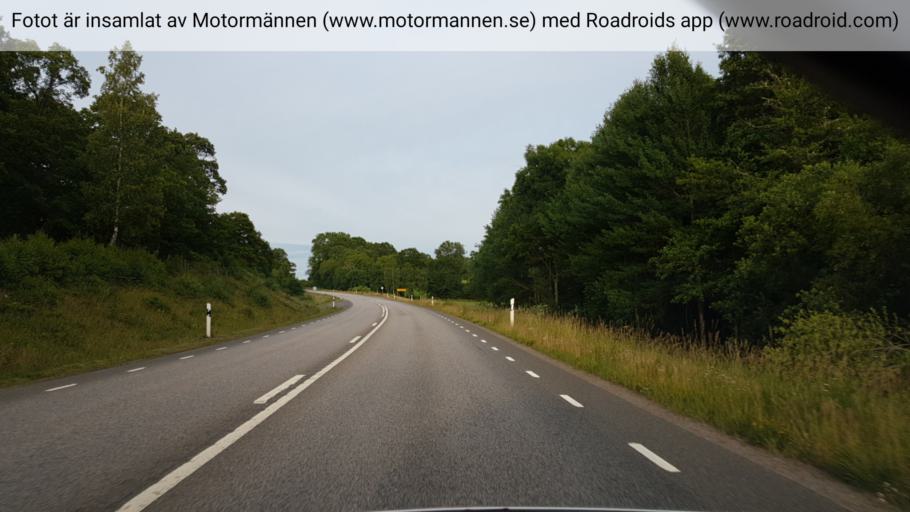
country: SE
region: Vaestra Goetaland
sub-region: Falkopings Kommun
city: Falkoeping
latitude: 58.2423
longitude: 13.5258
